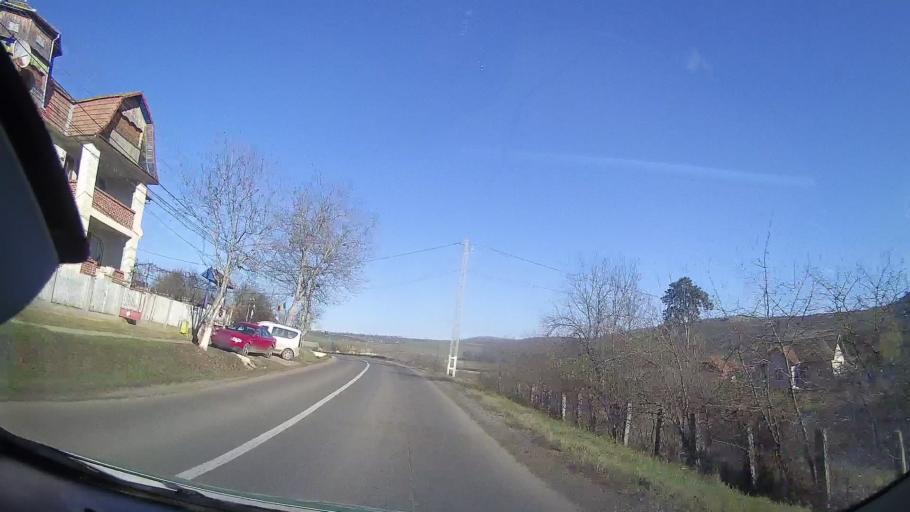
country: RO
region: Mures
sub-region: Comuna Sarmasu
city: Balda
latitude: 46.7303
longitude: 24.1453
